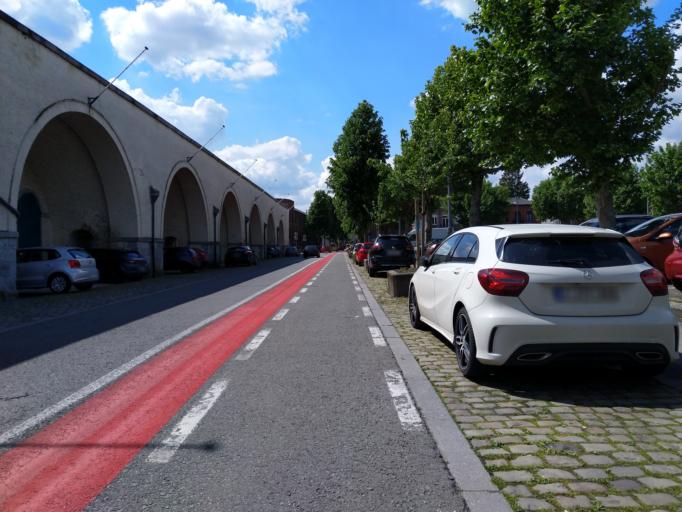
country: BE
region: Wallonia
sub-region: Province du Hainaut
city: Mons
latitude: 50.4480
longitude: 3.9464
